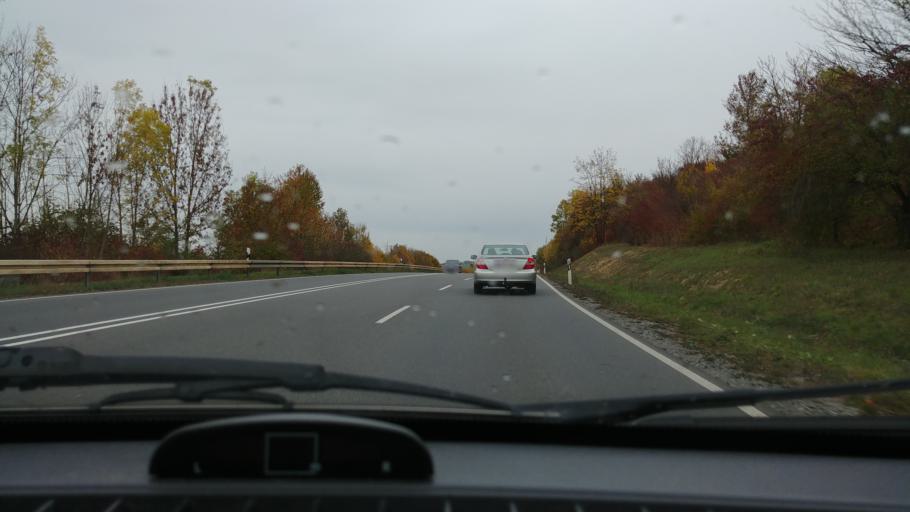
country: DE
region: Baden-Wuerttemberg
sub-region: Regierungsbezirk Stuttgart
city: Lauda-Konigshofen
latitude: 49.5838
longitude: 9.7073
